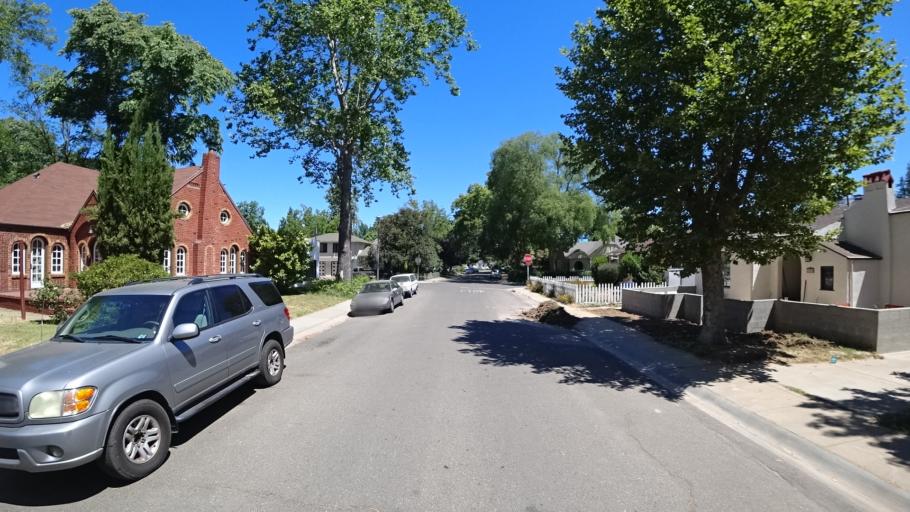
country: US
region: California
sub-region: Sacramento County
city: Sacramento
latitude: 38.5524
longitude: -121.4596
